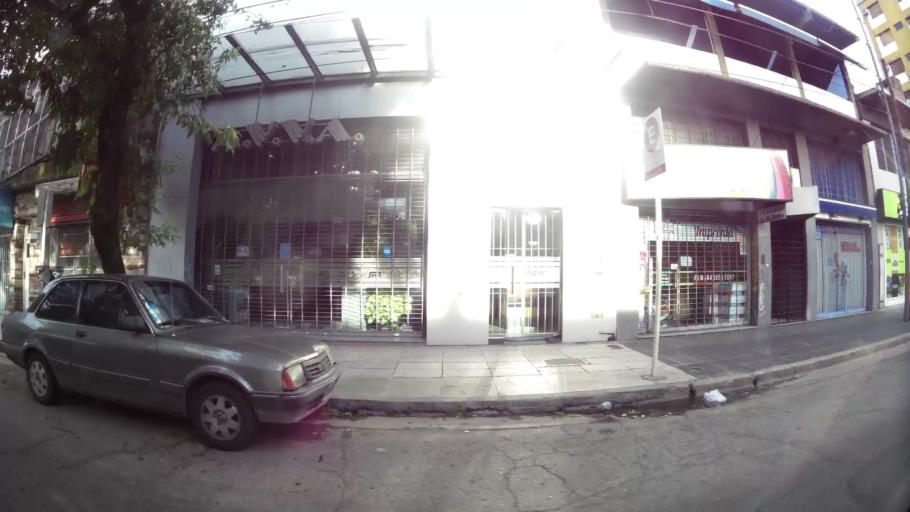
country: AR
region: Buenos Aires
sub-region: Partido de Moron
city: Moron
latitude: -34.6524
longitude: -58.6185
